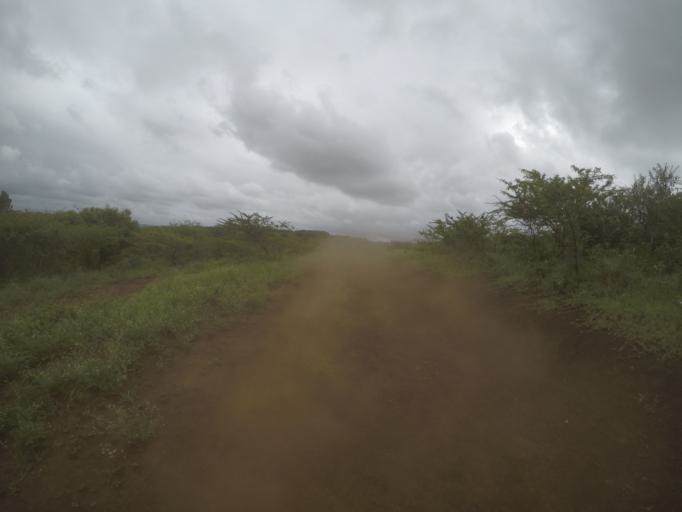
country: ZA
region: KwaZulu-Natal
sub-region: uThungulu District Municipality
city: Empangeni
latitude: -28.6019
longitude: 31.8520
